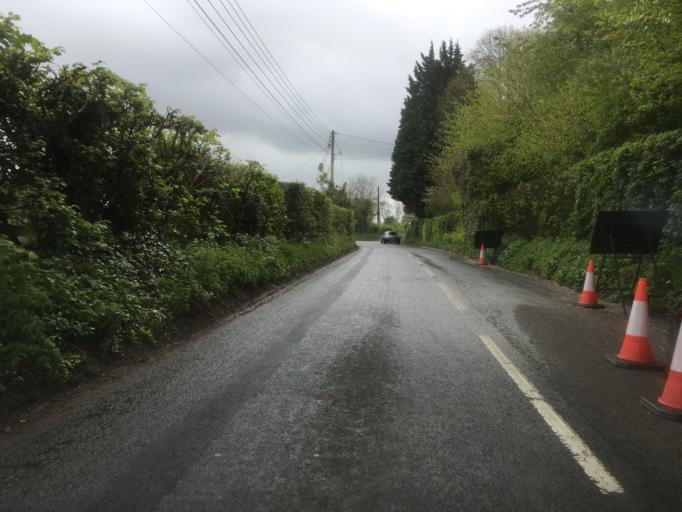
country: GB
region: England
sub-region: Bath and North East Somerset
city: Compton Martin
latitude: 51.3108
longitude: -2.6500
